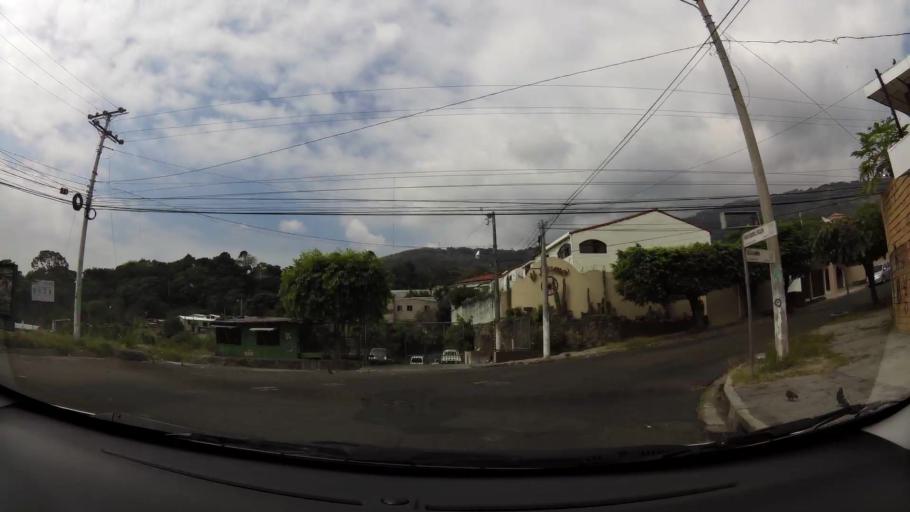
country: SV
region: La Libertad
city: Santa Tecla
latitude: 13.7045
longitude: -89.2591
